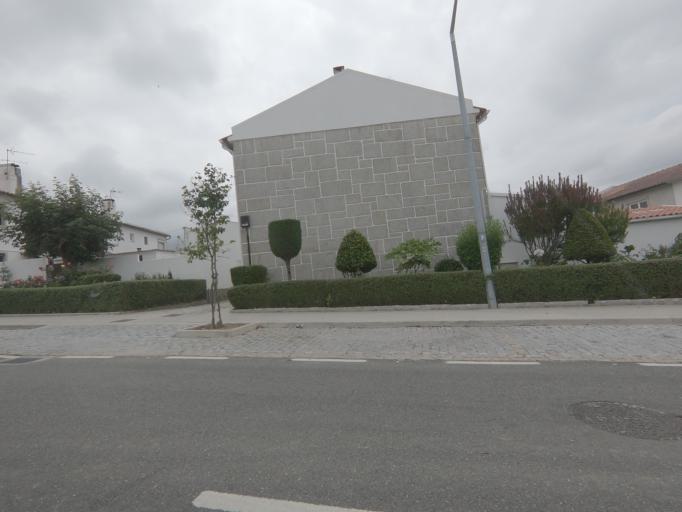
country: PT
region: Viana do Castelo
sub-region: Vila Nova de Cerveira
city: Vila Nova de Cerveira
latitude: 41.9446
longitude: -8.7415
